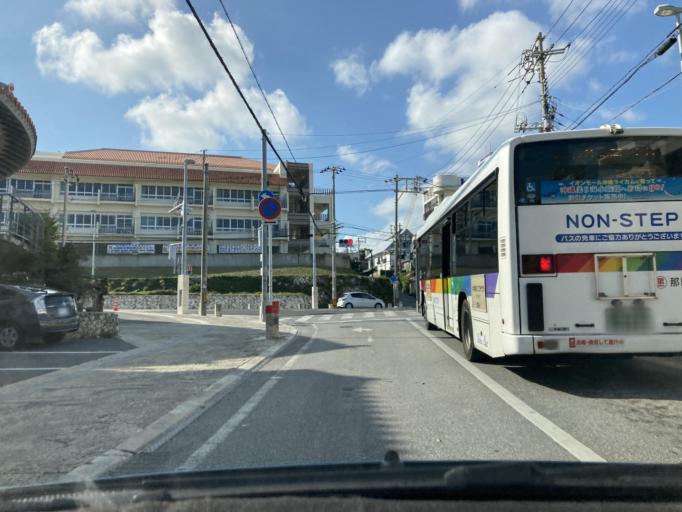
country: JP
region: Okinawa
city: Naha-shi
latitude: 26.2204
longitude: 127.7127
